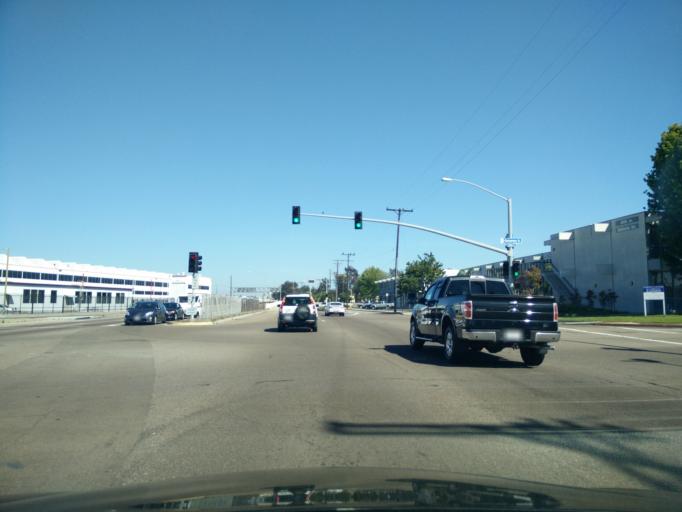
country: US
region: California
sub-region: San Diego County
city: San Diego
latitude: 32.7472
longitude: -117.1978
